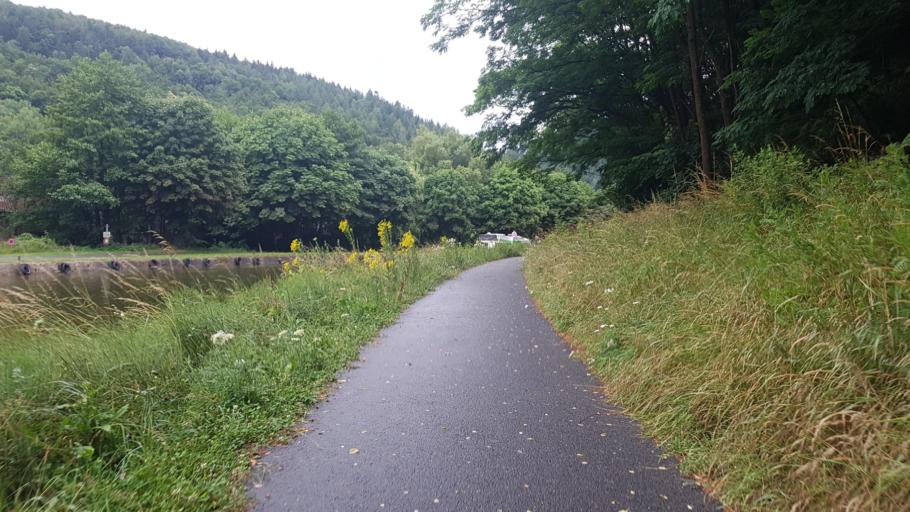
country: FR
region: Lorraine
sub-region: Departement de la Moselle
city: Phalsbourg
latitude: 48.7312
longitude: 7.2503
